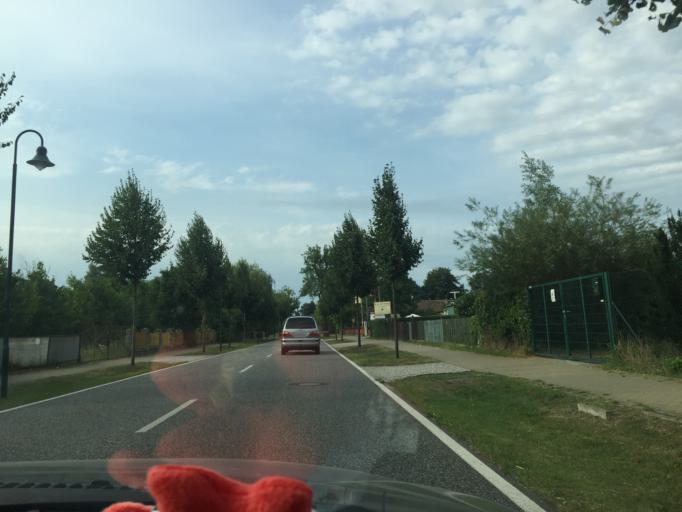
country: DE
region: Brandenburg
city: Liebenwalde
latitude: 52.8620
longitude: 13.3977
